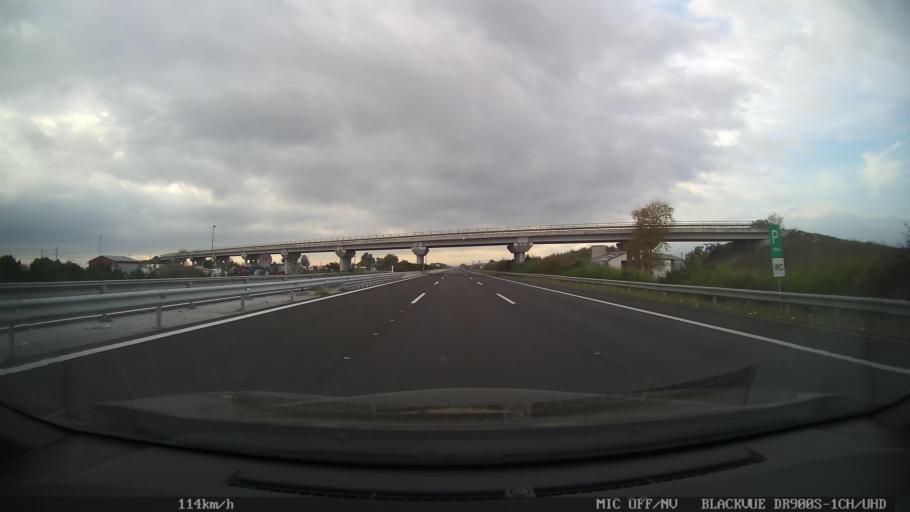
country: GR
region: Central Macedonia
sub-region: Nomos Pierias
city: Peristasi
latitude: 40.2436
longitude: 22.5350
